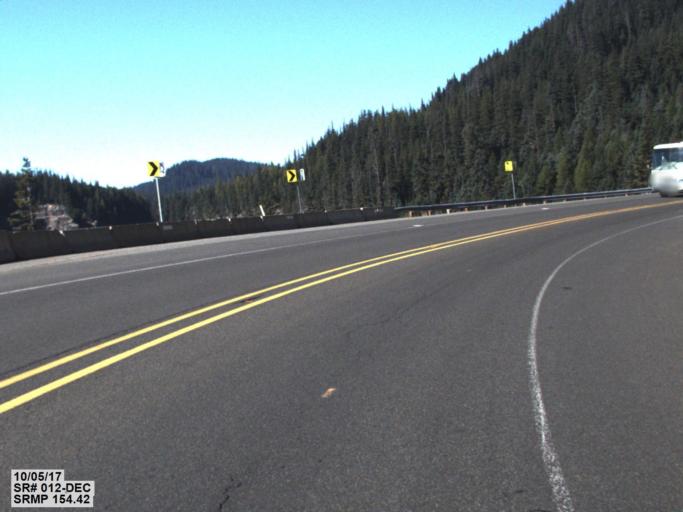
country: US
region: Washington
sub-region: Yakima County
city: Tieton
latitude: 46.6563
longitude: -121.3389
